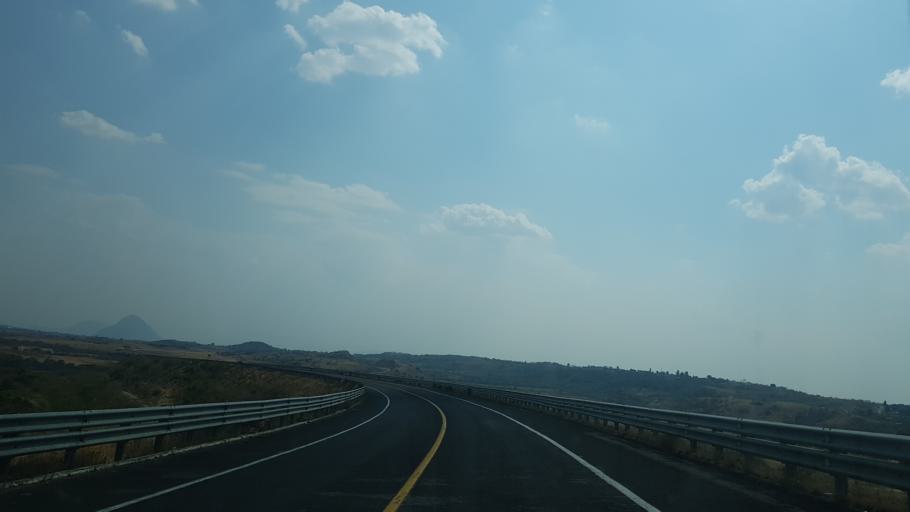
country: MX
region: Puebla
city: San Juan Amecac
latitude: 18.8186
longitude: -98.6935
